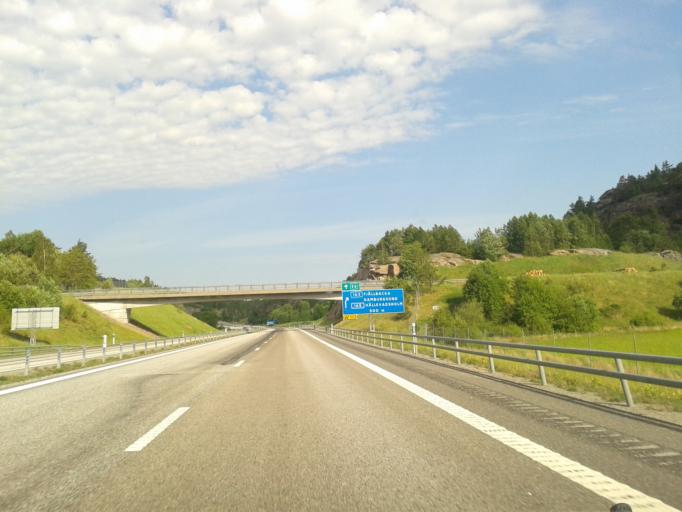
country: SE
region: Vaestra Goetaland
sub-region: Lysekils Kommun
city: Brastad
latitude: 58.5594
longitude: 11.4883
